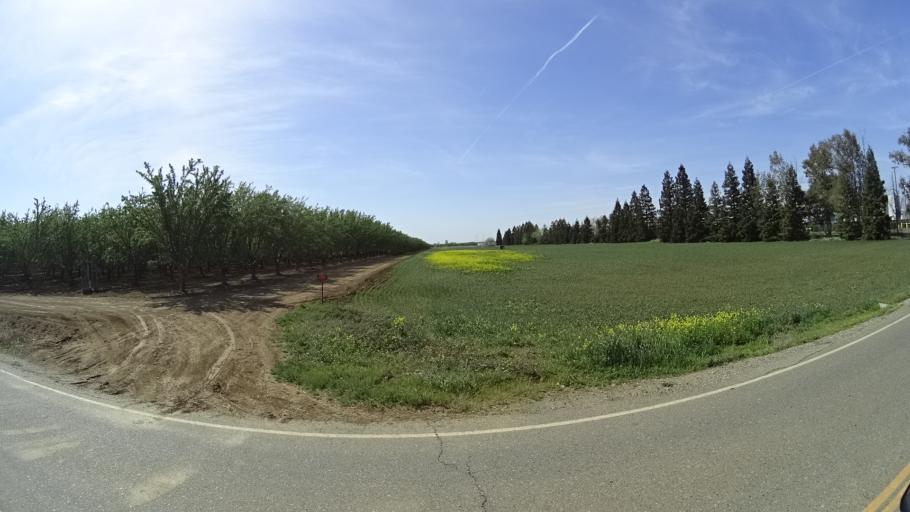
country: US
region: California
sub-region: Glenn County
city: Willows
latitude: 39.5386
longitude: -122.2587
